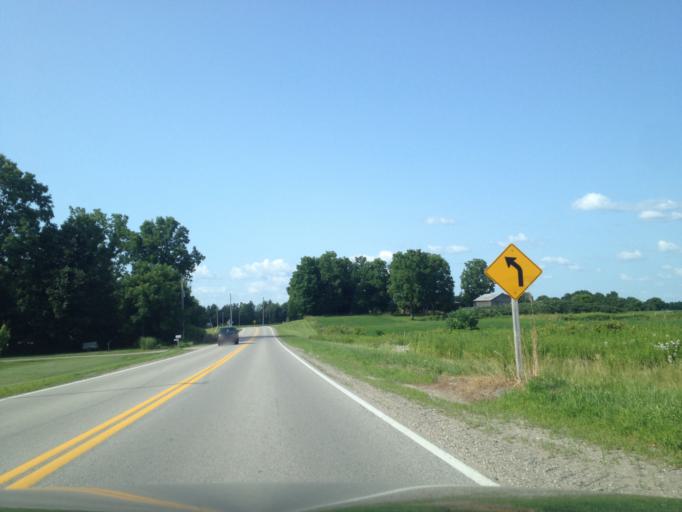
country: CA
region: Ontario
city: Aylmer
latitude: 42.7594
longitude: -80.8317
